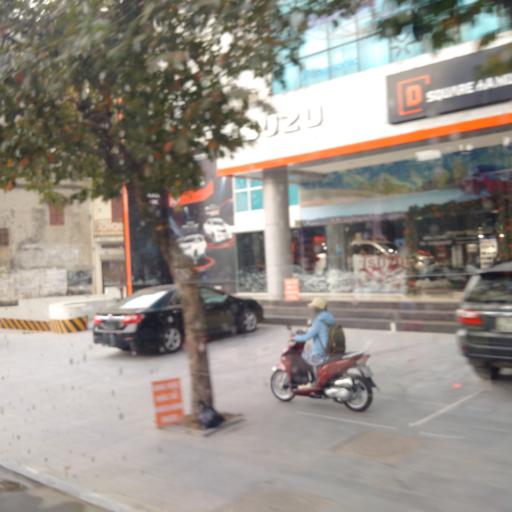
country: VN
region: Ha Noi
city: Cau Giay
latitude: 21.0461
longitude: 105.8003
